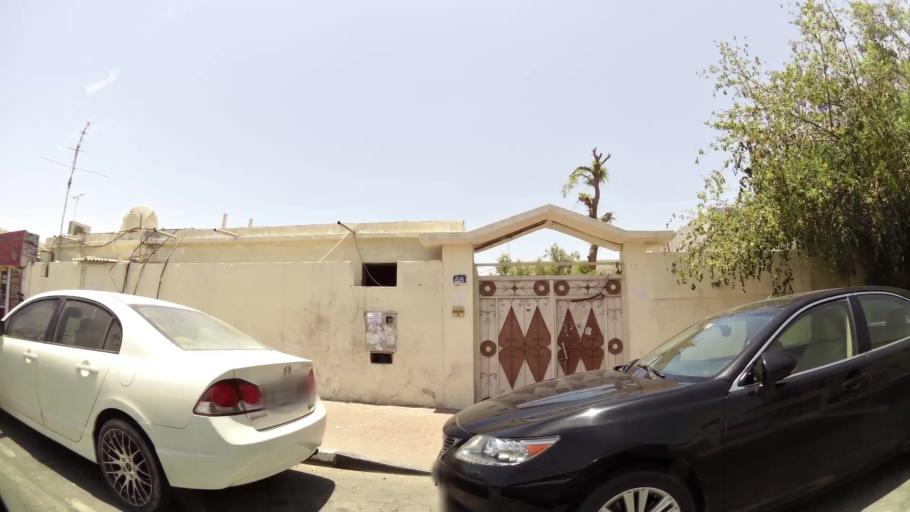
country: AE
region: Ash Shariqah
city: Sharjah
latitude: 25.2297
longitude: 55.2670
